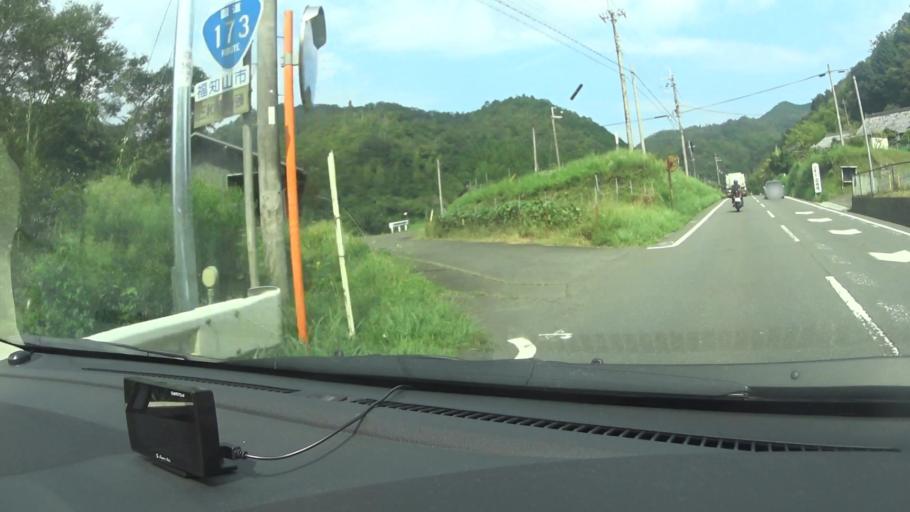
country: JP
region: Kyoto
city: Ayabe
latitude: 35.2544
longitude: 135.2772
